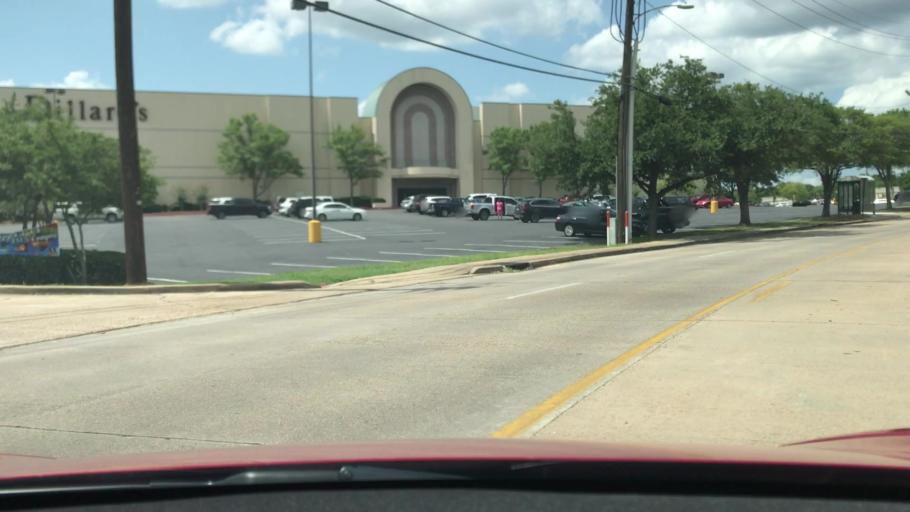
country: US
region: Louisiana
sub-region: Bossier Parish
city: Bossier City
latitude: 32.4800
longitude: -93.7527
